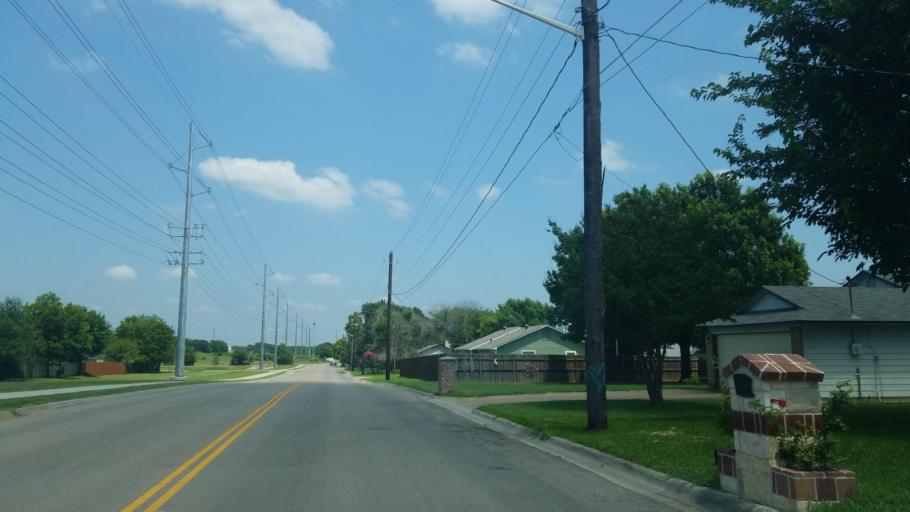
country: US
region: Texas
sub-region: Denton County
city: Denton
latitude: 33.2208
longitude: -97.0995
